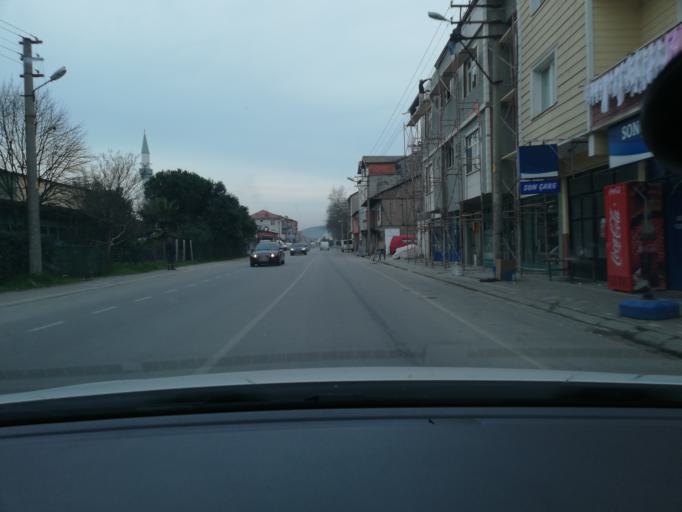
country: TR
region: Zonguldak
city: Caycuma
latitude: 41.4203
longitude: 32.0944
